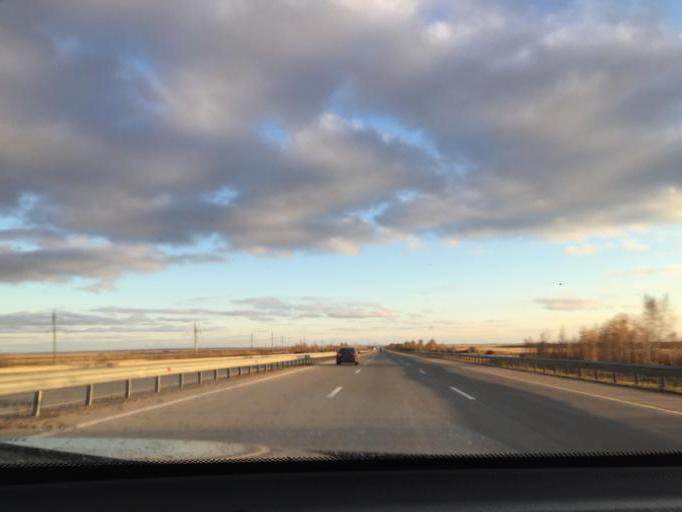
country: KZ
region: Astana Qalasy
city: Astana
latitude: 51.3372
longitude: 71.3416
